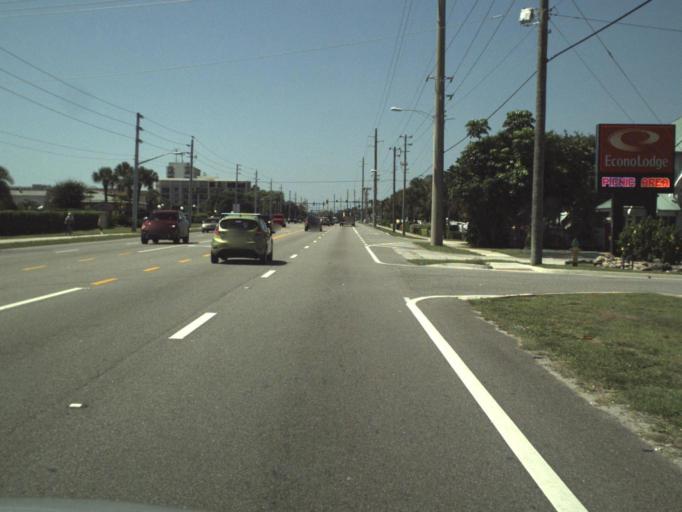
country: US
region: Florida
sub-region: Brevard County
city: Cocoa Beach
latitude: 28.3481
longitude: -80.6094
